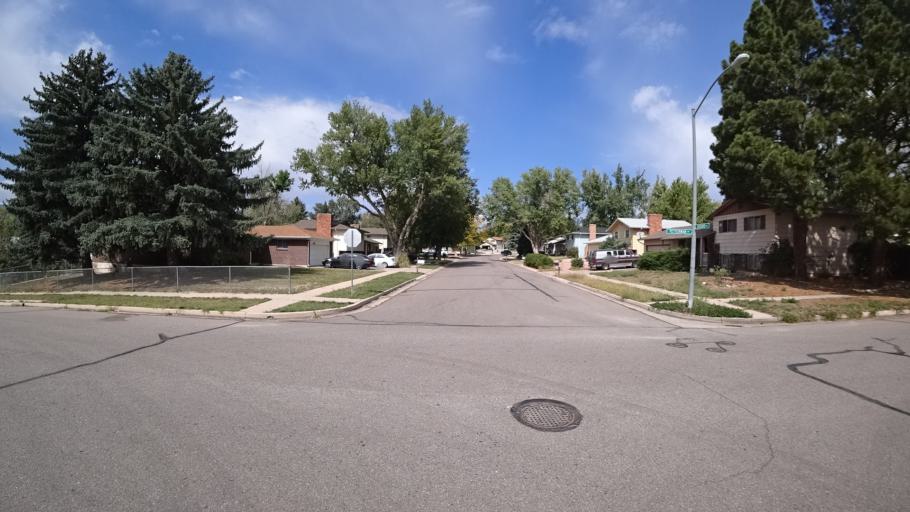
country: US
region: Colorado
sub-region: El Paso County
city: Cimarron Hills
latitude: 38.8524
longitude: -104.7424
